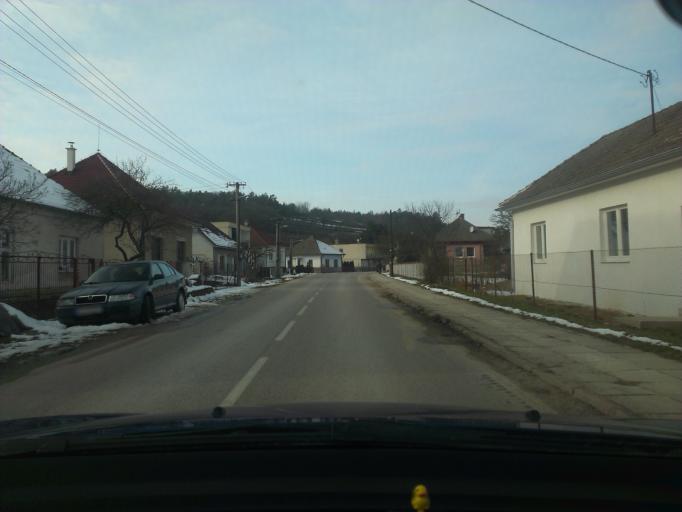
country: SK
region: Nitriansky
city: Stara Tura
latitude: 48.6969
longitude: 17.6865
